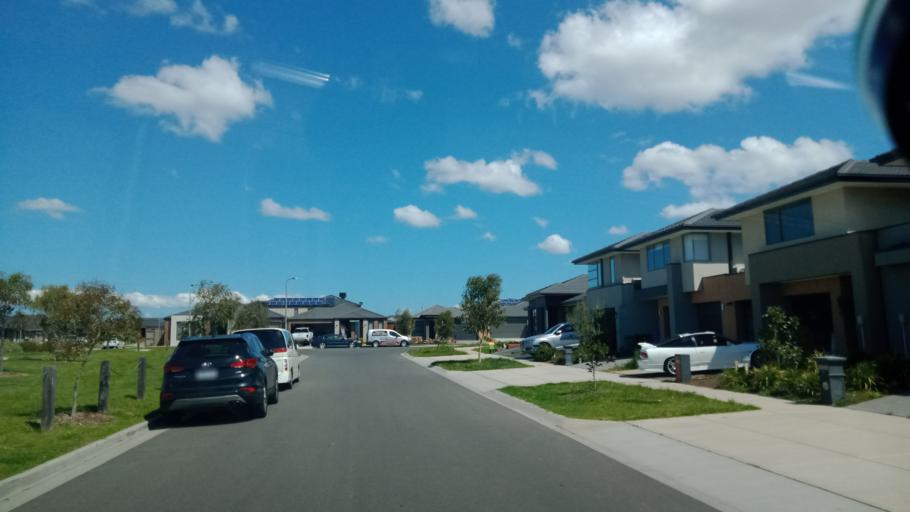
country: AU
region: Victoria
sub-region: Casey
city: Cranbourne West
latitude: -38.0990
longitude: 145.2470
